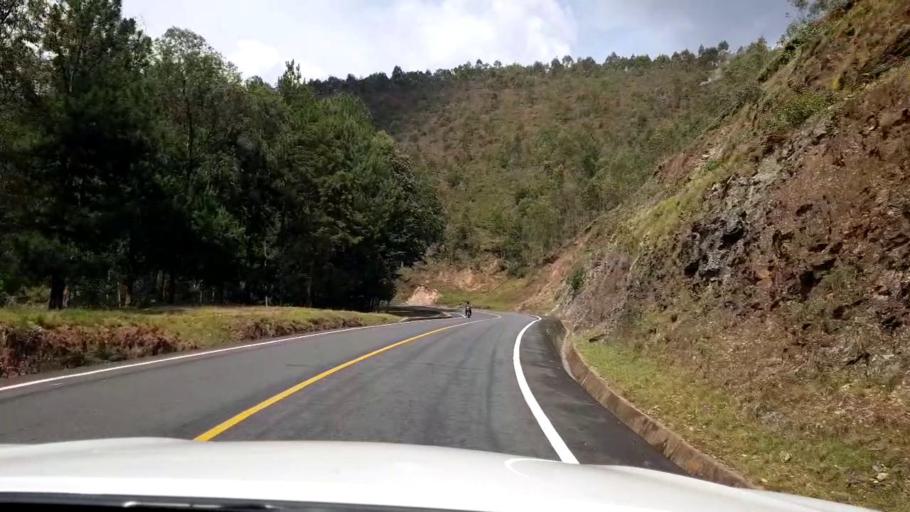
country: RW
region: Southern Province
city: Gitarama
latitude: -2.0304
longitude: 29.7170
